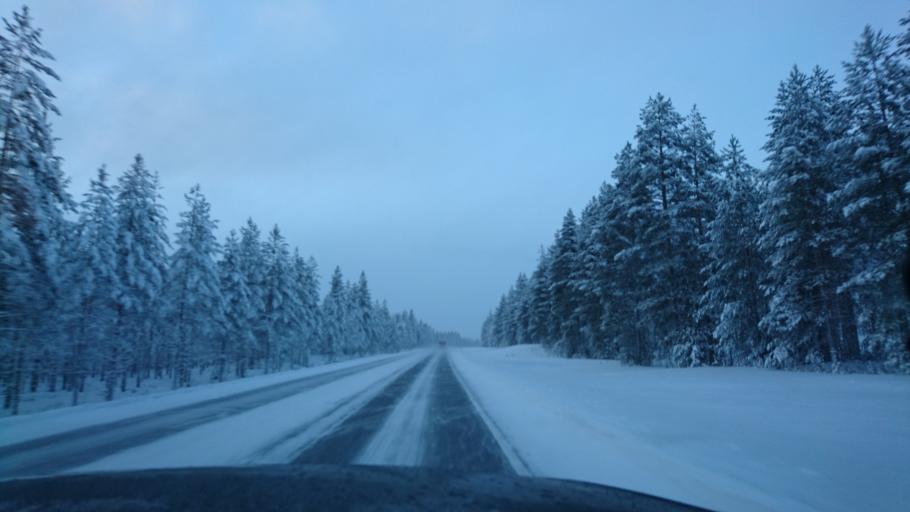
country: FI
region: Kainuu
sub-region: Kehys-Kainuu
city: Puolanka
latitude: 65.4340
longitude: 27.5828
